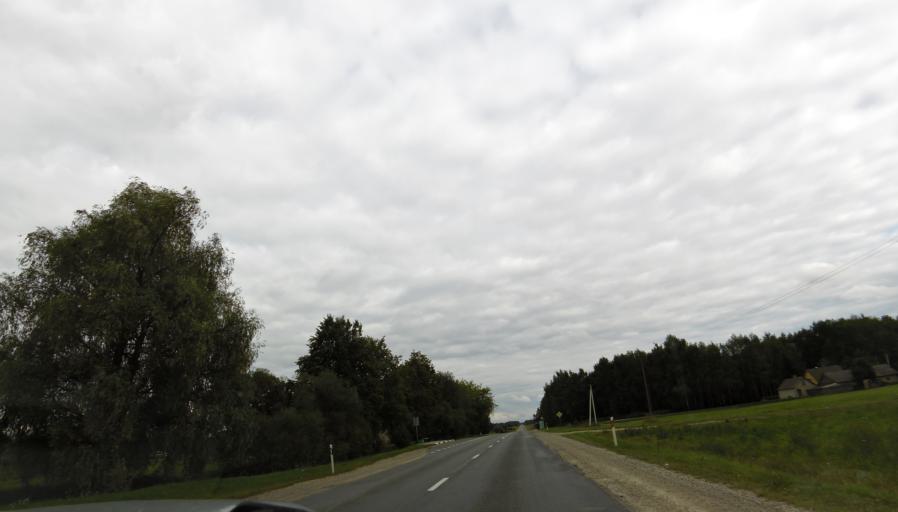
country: LT
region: Panevezys
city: Pasvalys
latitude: 56.0165
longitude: 24.2036
